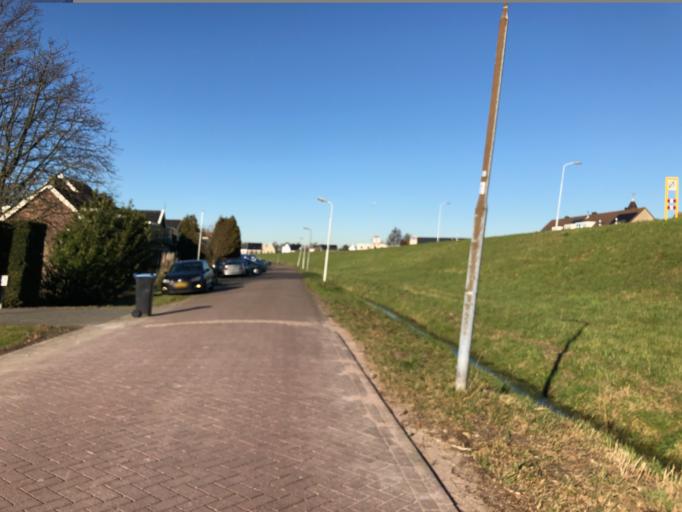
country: NL
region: North Holland
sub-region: Gemeente Zaanstad
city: Zaanstad
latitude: 52.4318
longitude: 4.7796
